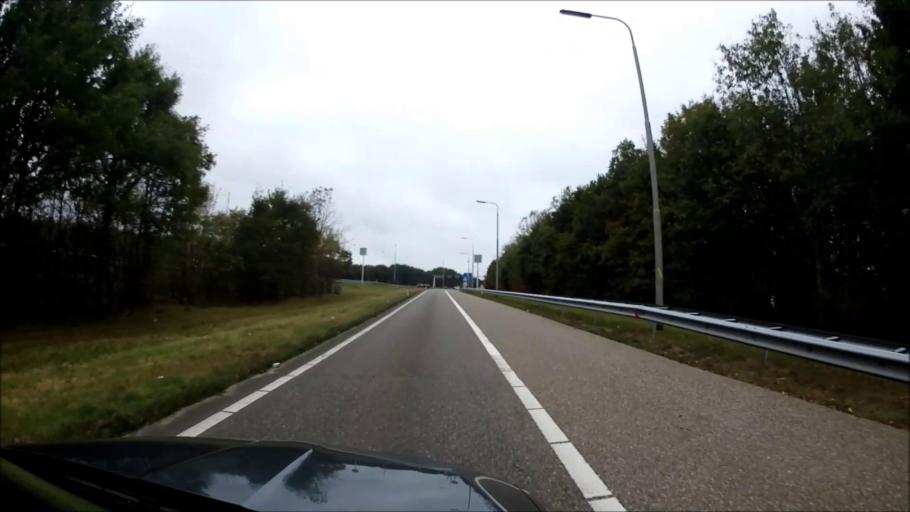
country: NL
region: North Holland
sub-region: Gemeente Naarden
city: Naarden
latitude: 52.3064
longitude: 5.1419
